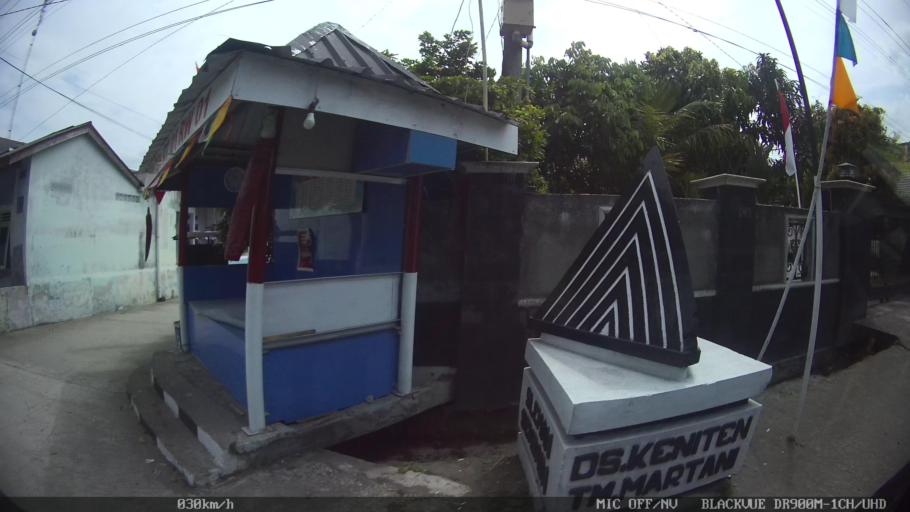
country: ID
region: Central Java
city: Candi Prambanan
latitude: -7.7541
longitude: 110.4807
